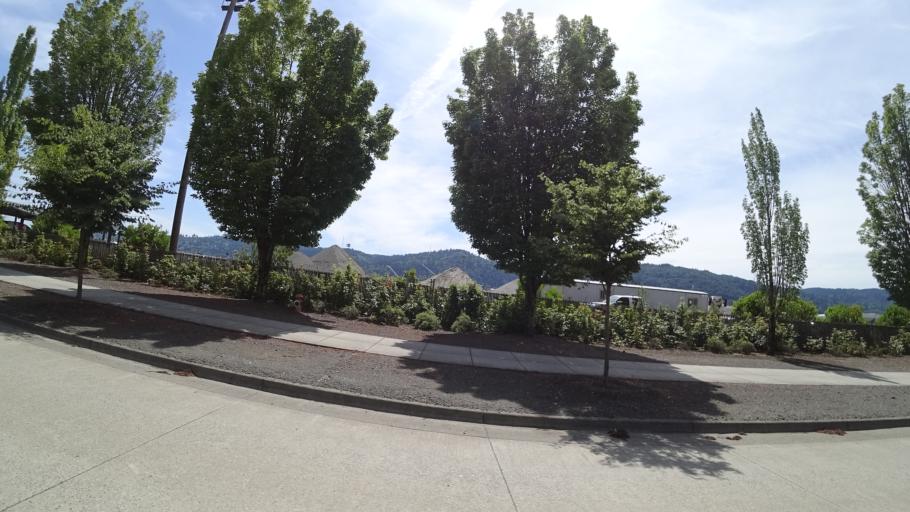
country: US
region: Oregon
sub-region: Multnomah County
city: Portland
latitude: 45.5607
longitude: -122.7124
